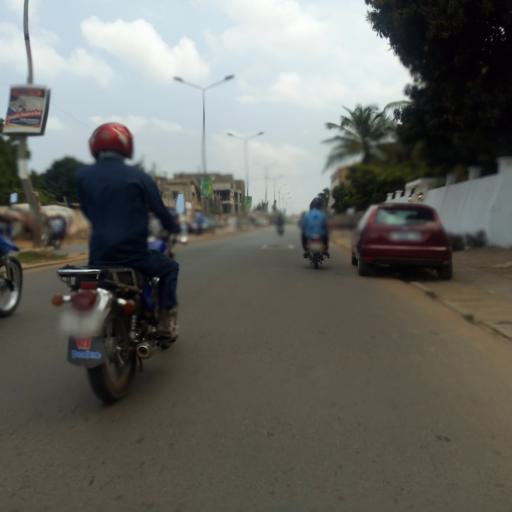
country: TG
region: Maritime
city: Lome
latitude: 6.1978
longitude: 1.1786
